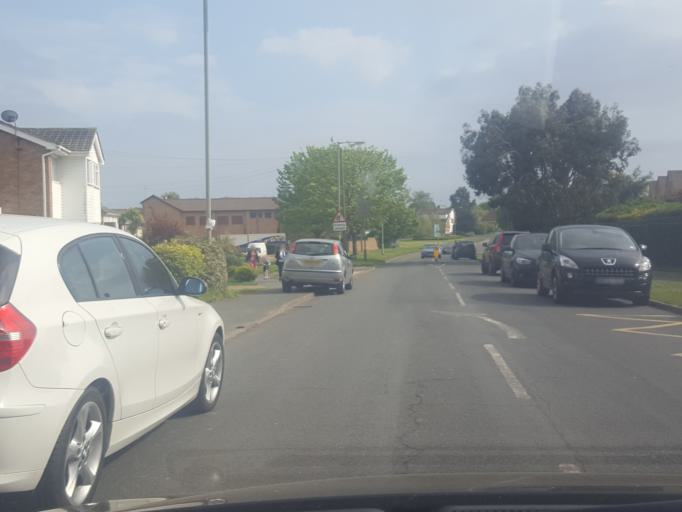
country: GB
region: England
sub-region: Essex
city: Frinton-on-Sea
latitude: 51.8458
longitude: 1.2478
